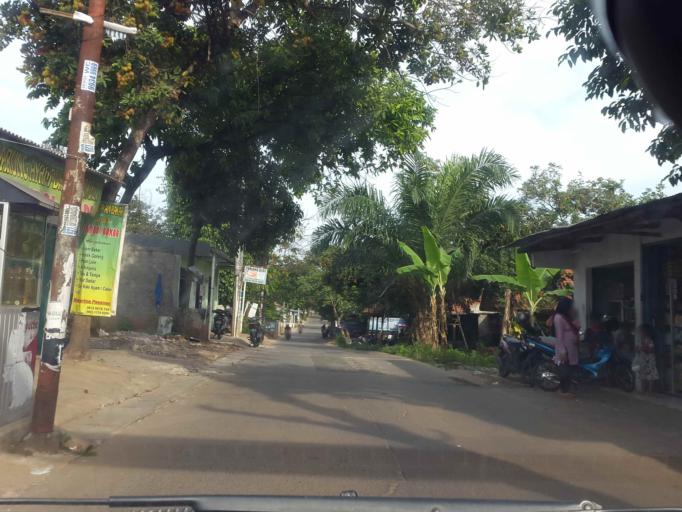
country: ID
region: West Java
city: Serpong
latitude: -6.2805
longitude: 106.6785
